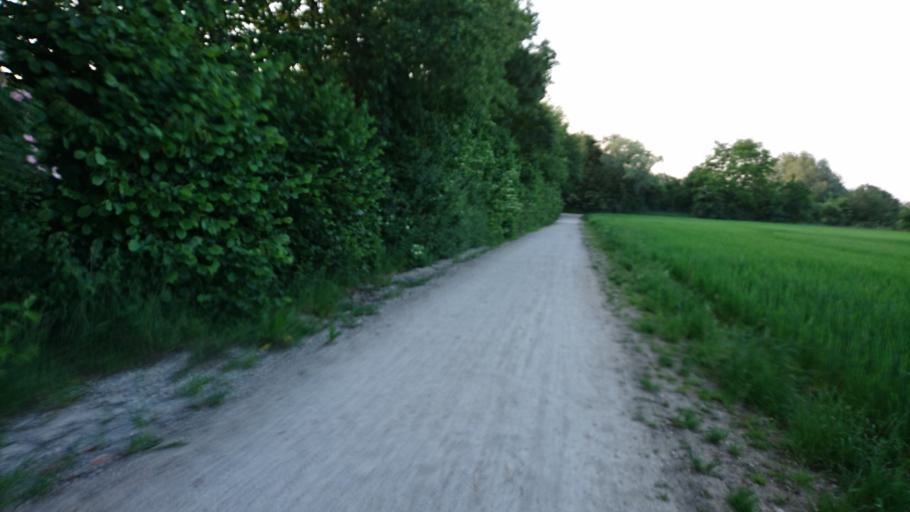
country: DE
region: Bavaria
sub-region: Upper Bavaria
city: Pliening
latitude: 48.1853
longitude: 11.8029
